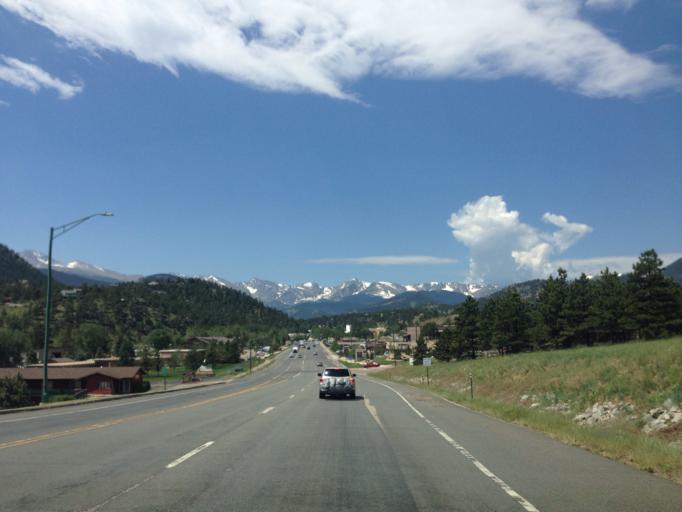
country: US
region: Colorado
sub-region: Larimer County
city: Estes Park
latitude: 40.3813
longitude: -105.5107
